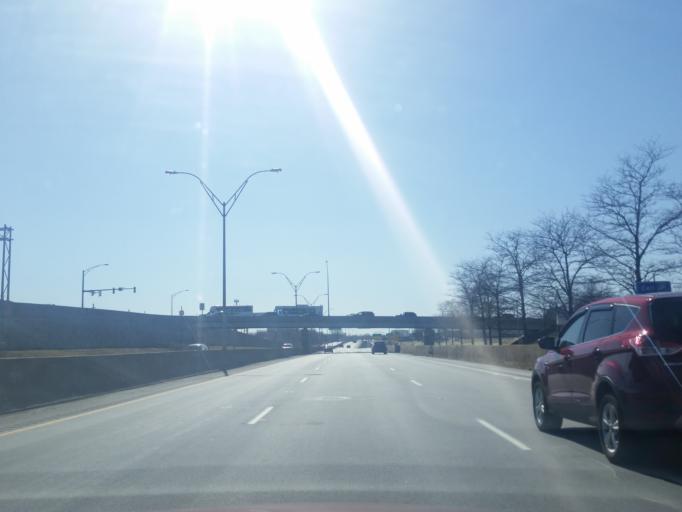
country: US
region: Ohio
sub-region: Cuyahoga County
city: Brook Park
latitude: 41.4088
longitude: -81.8335
